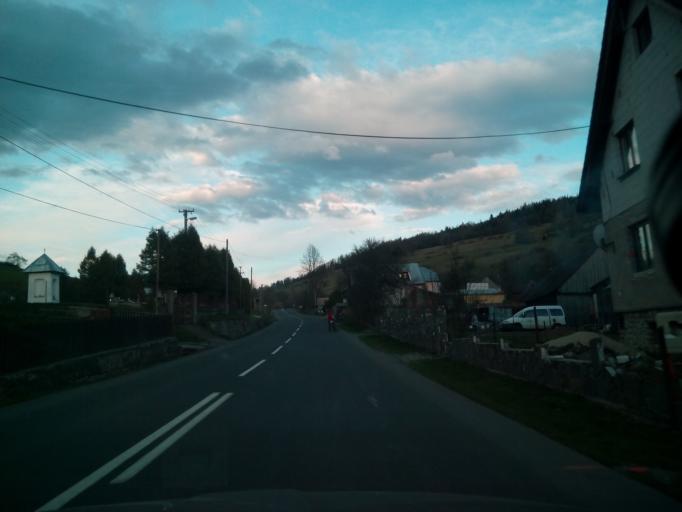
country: SK
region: Presovsky
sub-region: Okres Poprad
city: Zdiar
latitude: 49.2972
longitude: 20.3839
